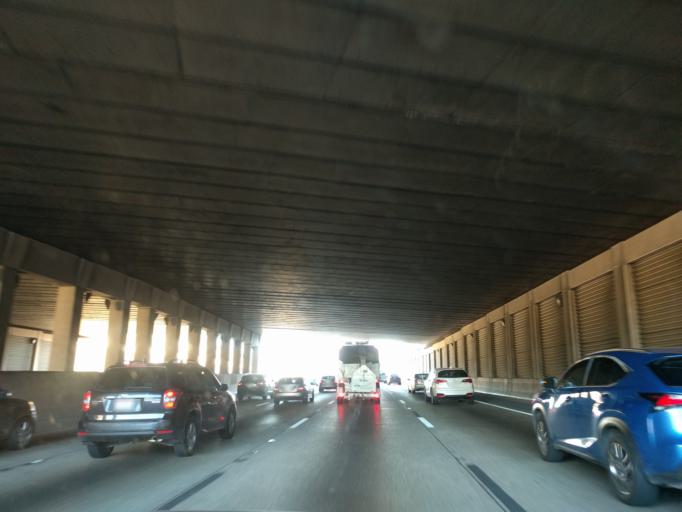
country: US
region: Texas
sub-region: Dallas County
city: Highland Park
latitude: 32.8508
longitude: -96.7714
